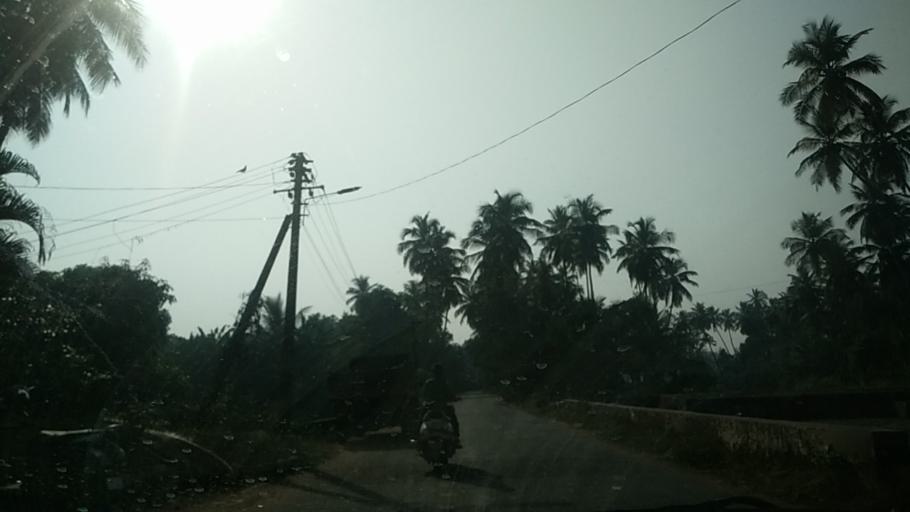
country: IN
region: Goa
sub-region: North Goa
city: Pernem
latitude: 15.7328
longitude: 73.7617
